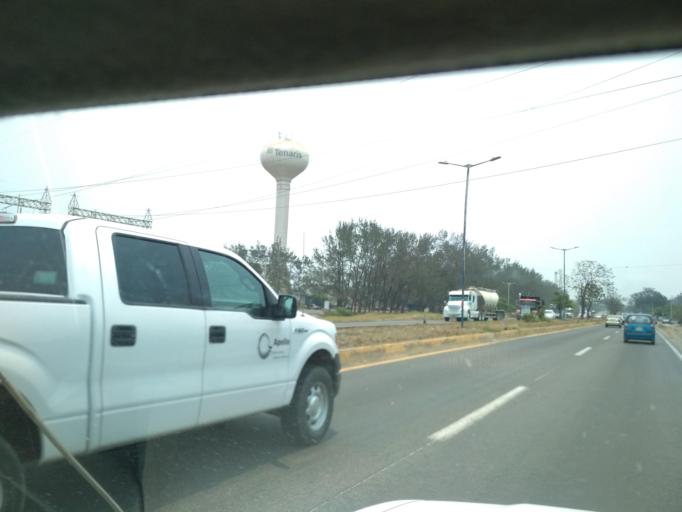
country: MX
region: Veracruz
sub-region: Veracruz
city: Oasis
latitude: 19.1764
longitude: -96.2424
